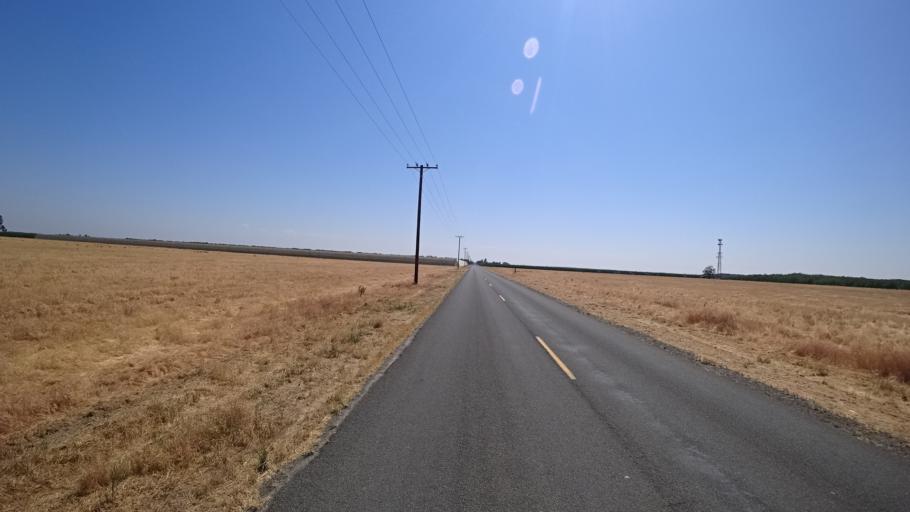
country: US
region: California
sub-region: Kings County
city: Lucerne
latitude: 36.3719
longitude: -119.6305
